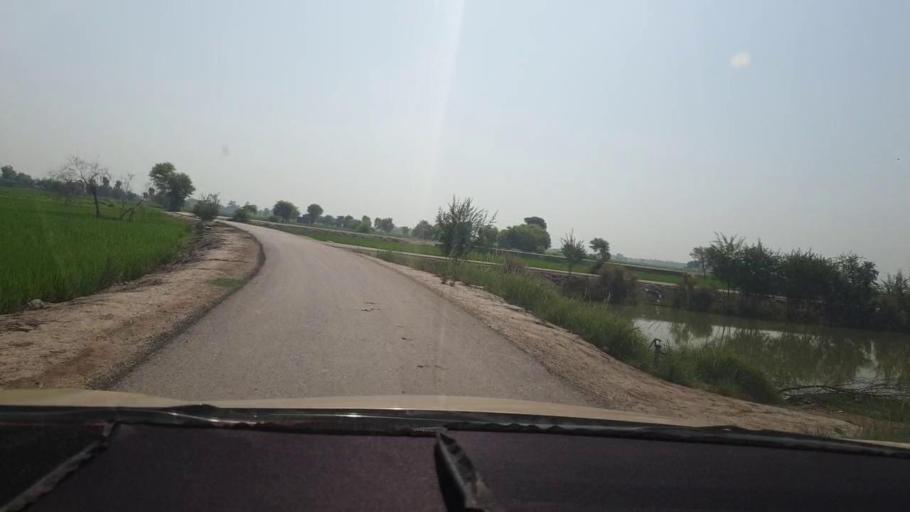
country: PK
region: Sindh
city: Kambar
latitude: 27.5723
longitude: 68.0427
